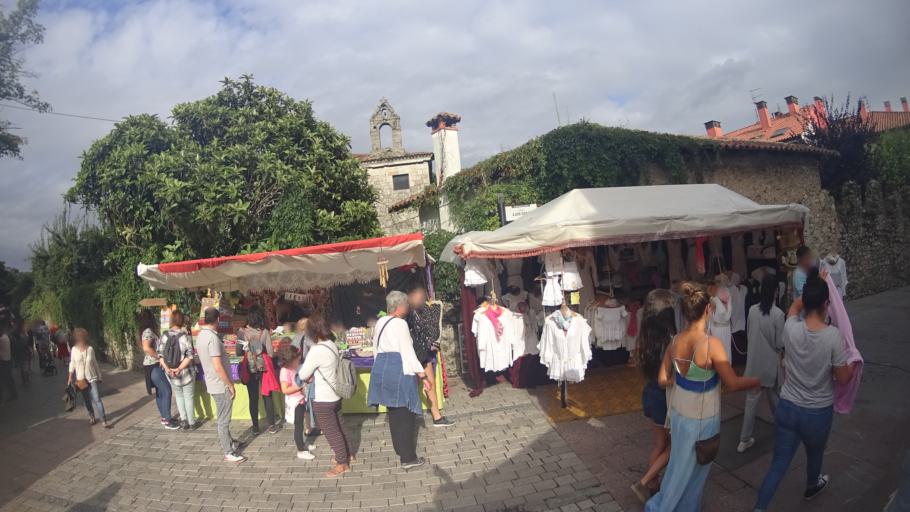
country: ES
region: Asturias
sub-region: Province of Asturias
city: Llanes
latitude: 43.4216
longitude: -4.7537
